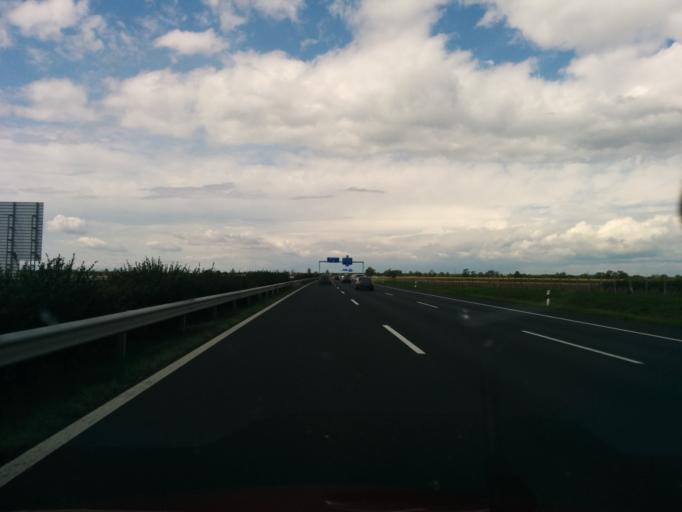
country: HU
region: Gyor-Moson-Sopron
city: Mosonmagyarovar
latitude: 47.8843
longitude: 17.1917
